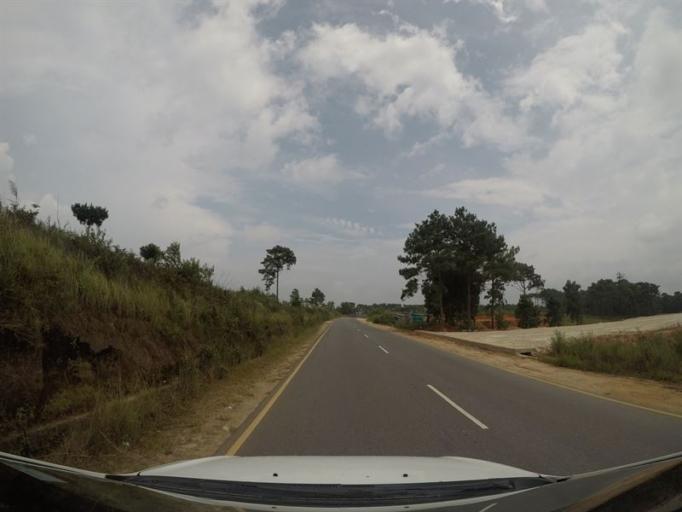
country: IN
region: Meghalaya
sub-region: East Khasi Hills
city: Shillong
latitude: 25.4907
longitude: 92.1867
